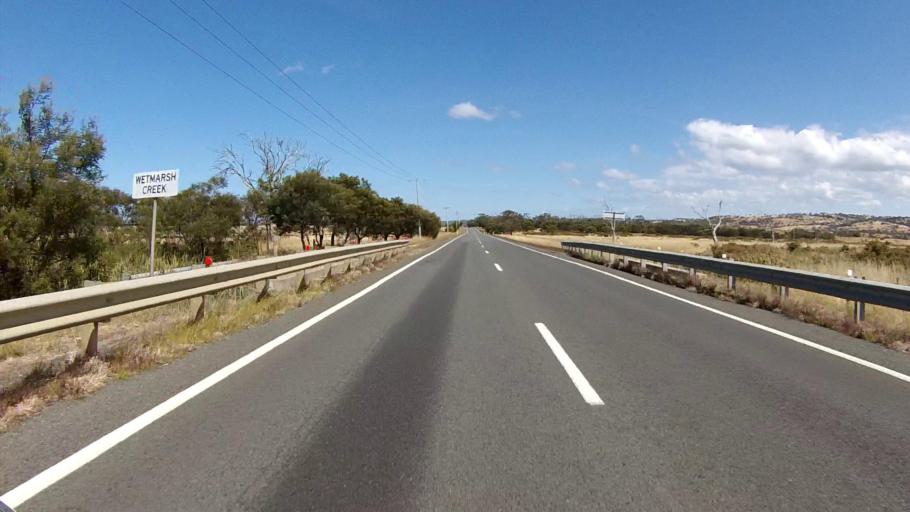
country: AU
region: Tasmania
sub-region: Break O'Day
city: St Helens
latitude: -42.0910
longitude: 148.0661
